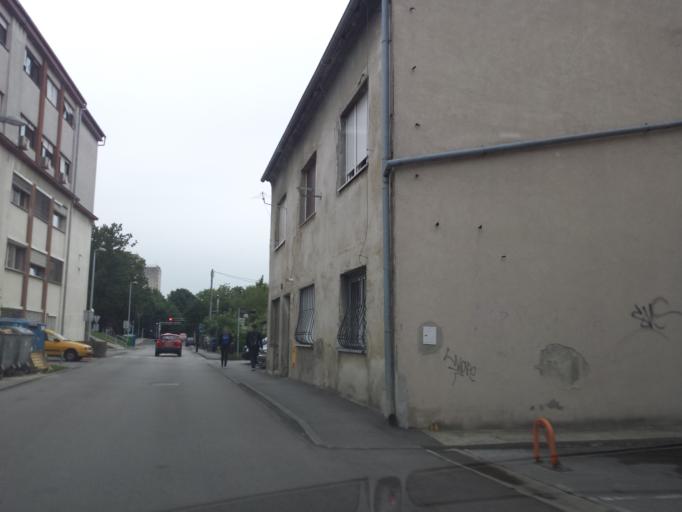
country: HR
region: Grad Zagreb
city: Zagreb - Centar
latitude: 45.8013
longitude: 15.9675
